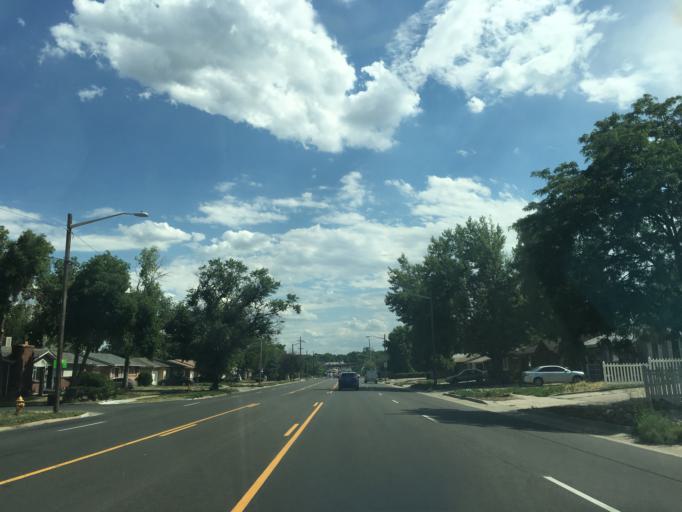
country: US
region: Colorado
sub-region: Arapahoe County
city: Sheridan
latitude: 39.6602
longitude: -105.0534
